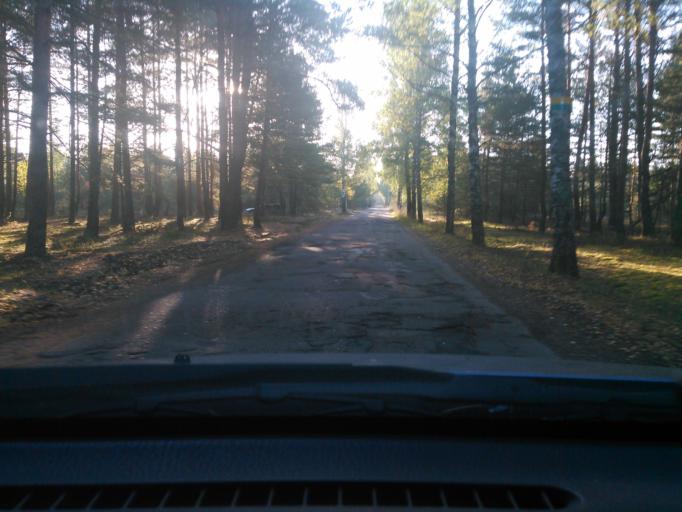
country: LV
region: Adazi
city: Adazi
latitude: 57.1065
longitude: 24.3704
